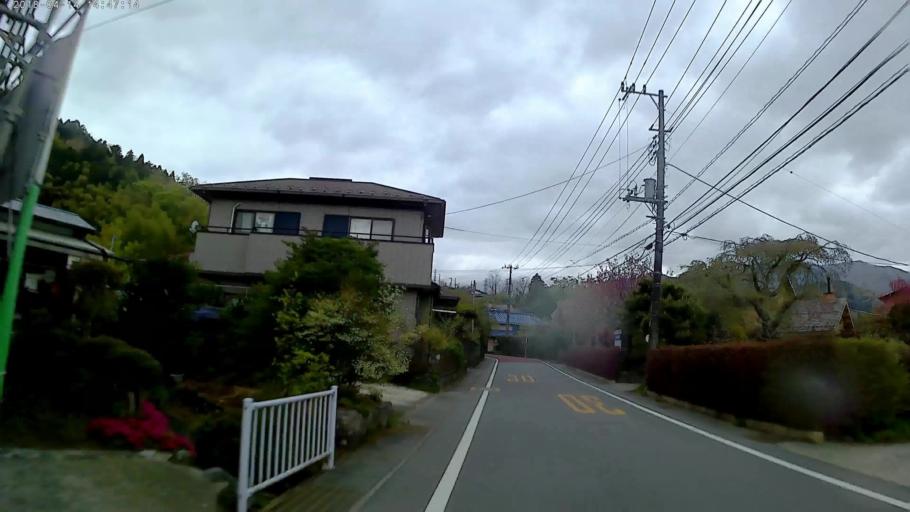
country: JP
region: Shizuoka
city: Gotemba
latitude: 35.3654
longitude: 138.9822
